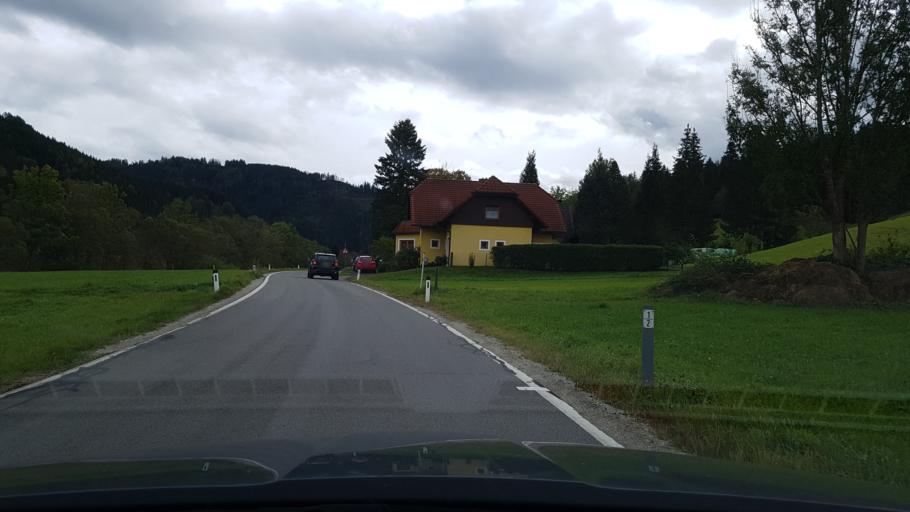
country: AT
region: Styria
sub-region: Politischer Bezirk Bruck-Muerzzuschlag
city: Allerheiligen im Muerztal
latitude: 47.4739
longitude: 15.4145
